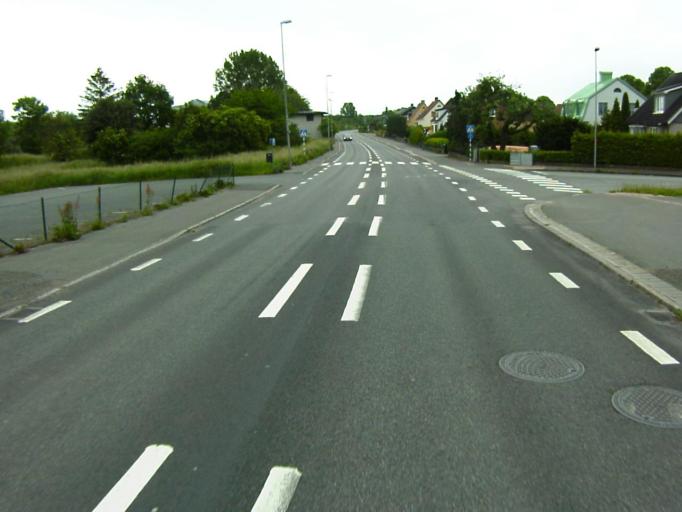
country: SE
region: Skane
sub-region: Kristianstads Kommun
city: Kristianstad
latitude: 56.0168
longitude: 14.1492
